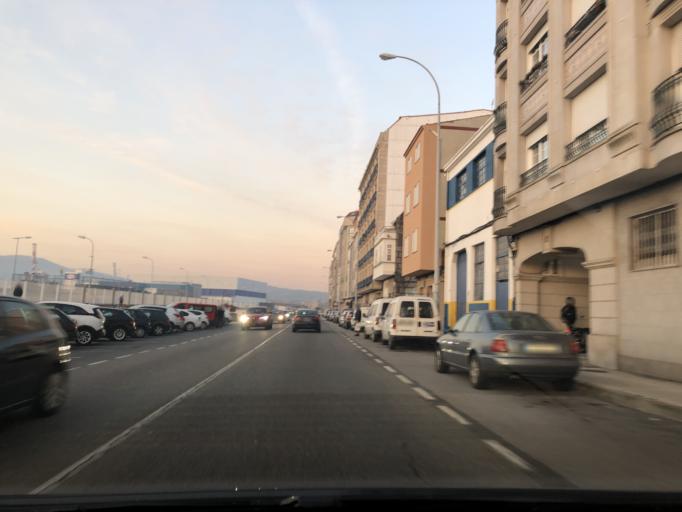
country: ES
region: Galicia
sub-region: Provincia de Pontevedra
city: Marin
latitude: 42.3955
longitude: -8.6931
